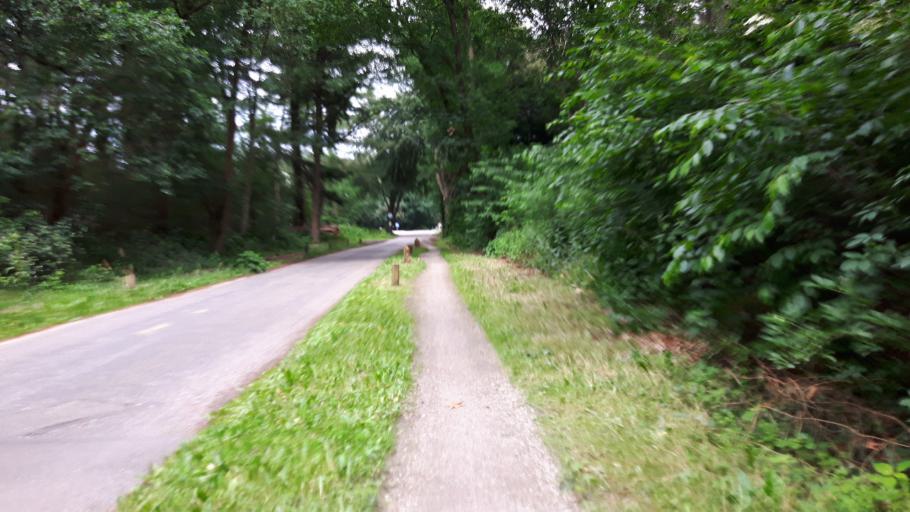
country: NL
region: Utrecht
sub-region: Gemeente De Bilt
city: De Bilt
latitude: 52.1380
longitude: 5.1874
